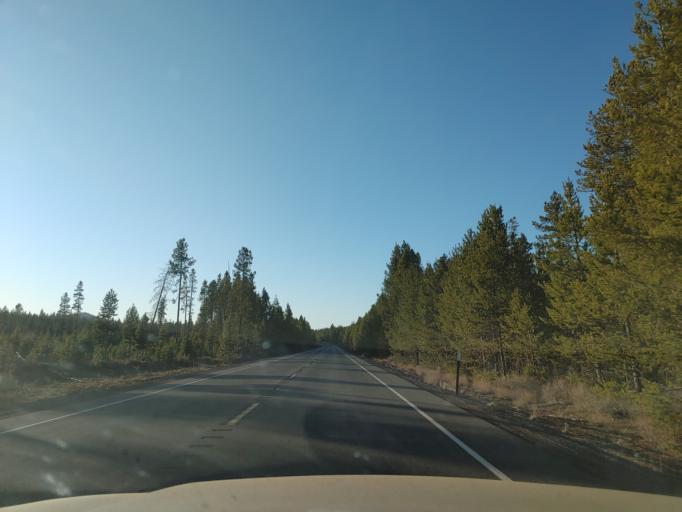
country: US
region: Oregon
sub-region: Deschutes County
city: La Pine
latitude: 43.4176
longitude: -121.8381
